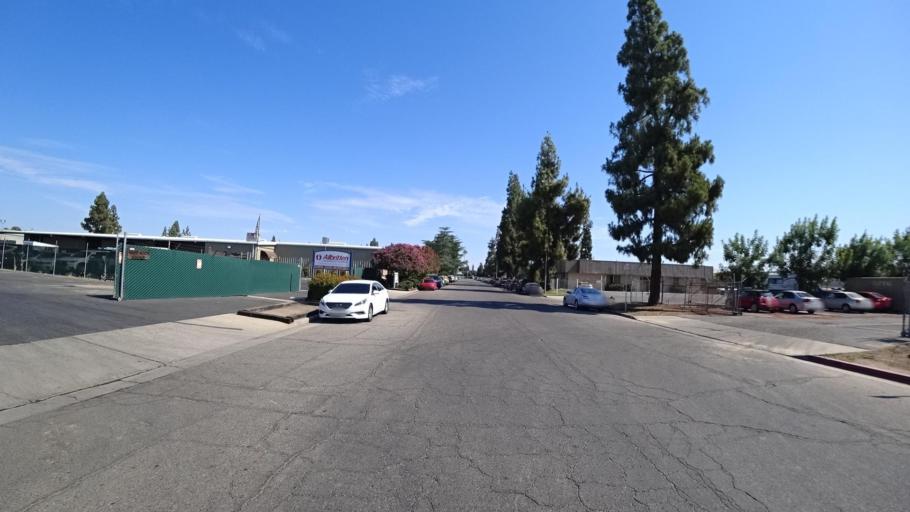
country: US
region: California
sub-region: Fresno County
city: Tarpey Village
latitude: 36.7741
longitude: -119.6975
